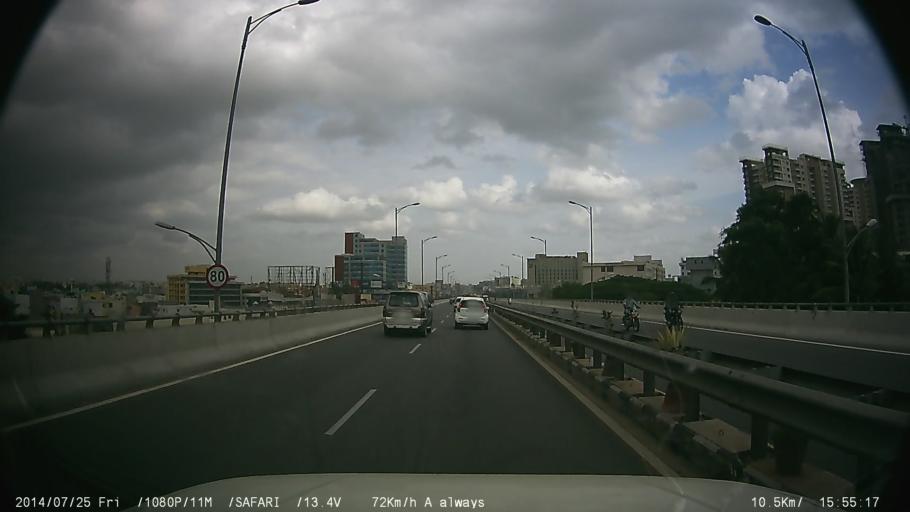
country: IN
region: Karnataka
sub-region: Bangalore Urban
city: Bangalore
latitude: 12.9043
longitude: 77.6307
